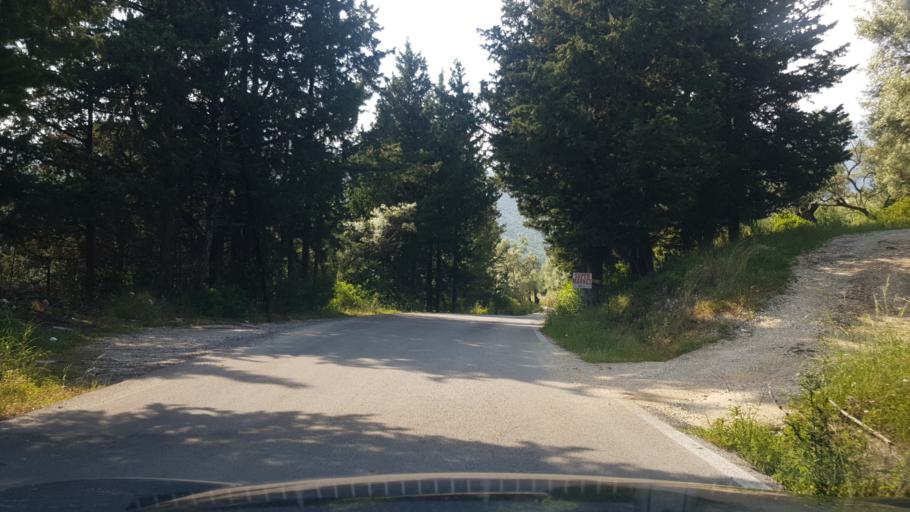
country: GR
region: Ionian Islands
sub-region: Lefkada
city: Nidri
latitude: 38.6538
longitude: 20.7033
